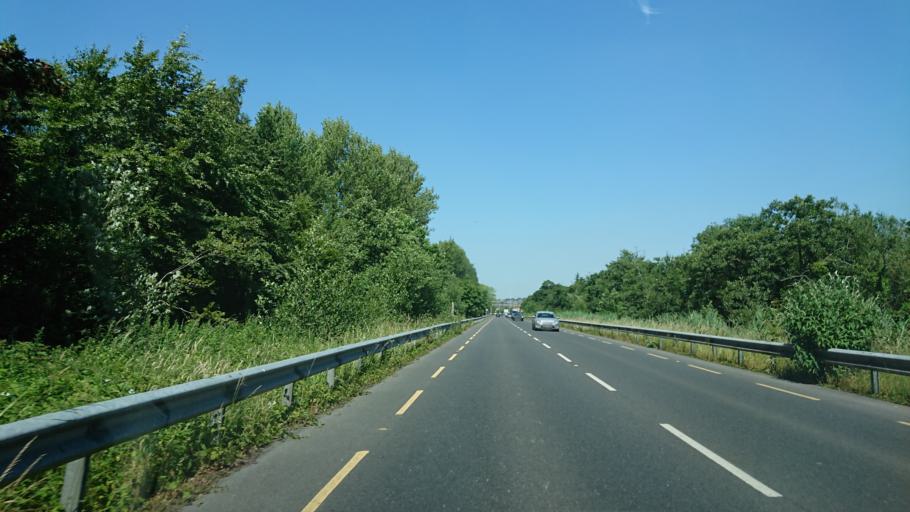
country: IE
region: Munster
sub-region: Waterford
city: Waterford
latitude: 52.2414
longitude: -7.1209
